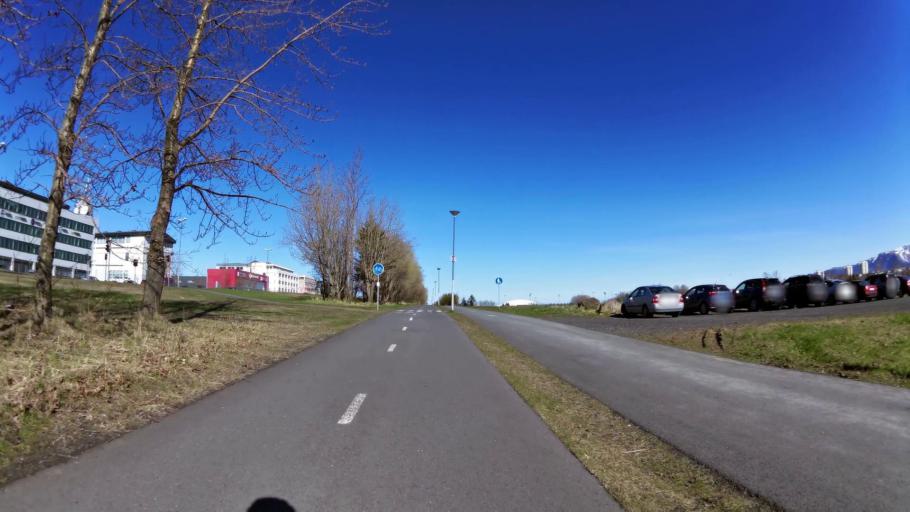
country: IS
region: Capital Region
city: Reykjavik
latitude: 64.1358
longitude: -21.8723
